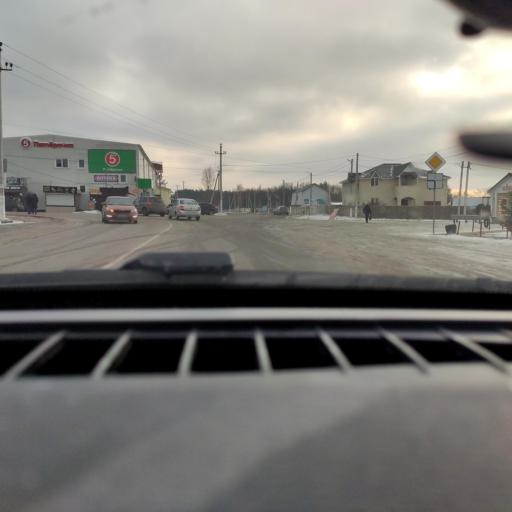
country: RU
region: Voronezj
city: Podgornoye
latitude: 51.7906
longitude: 39.1460
